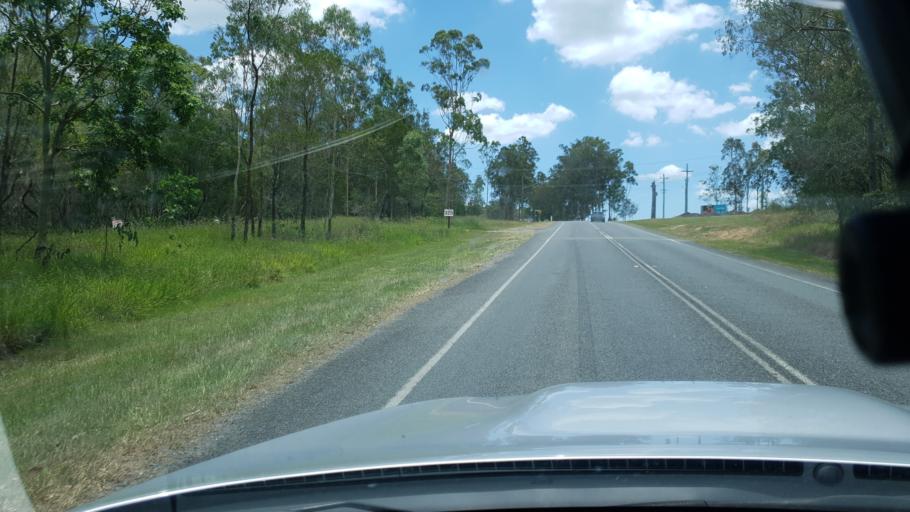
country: AU
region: Queensland
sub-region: Logan
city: North Maclean
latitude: -27.7452
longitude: 152.9855
